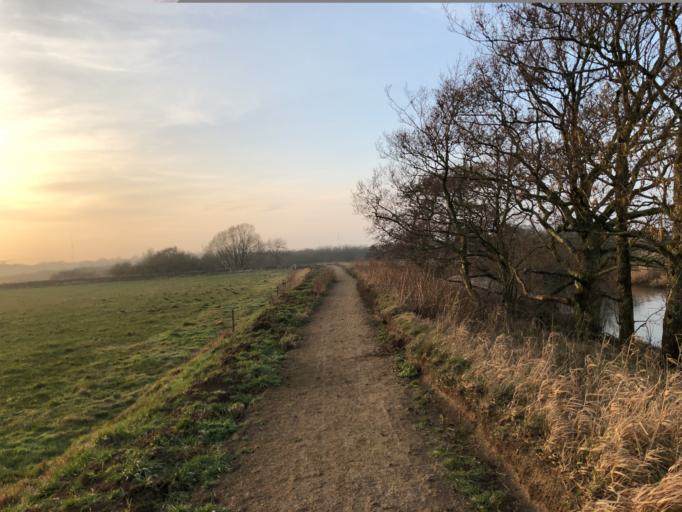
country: DK
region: Central Jutland
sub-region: Holstebro Kommune
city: Ulfborg
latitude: 56.3427
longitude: 8.3652
